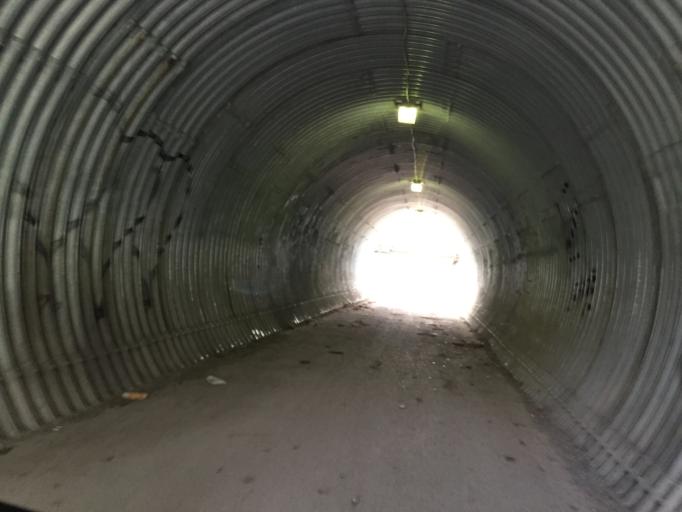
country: SE
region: Dalarna
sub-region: Ludvika Kommun
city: Ludvika
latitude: 60.1340
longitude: 15.1765
